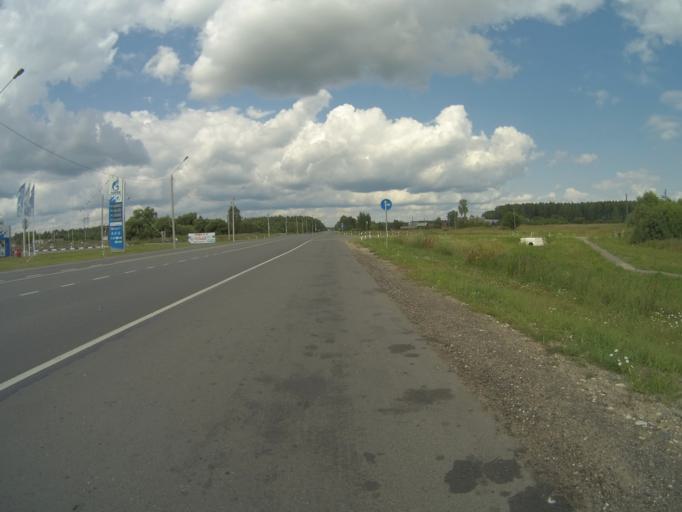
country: RU
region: Vladimir
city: Kideksha
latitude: 56.5893
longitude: 40.5554
